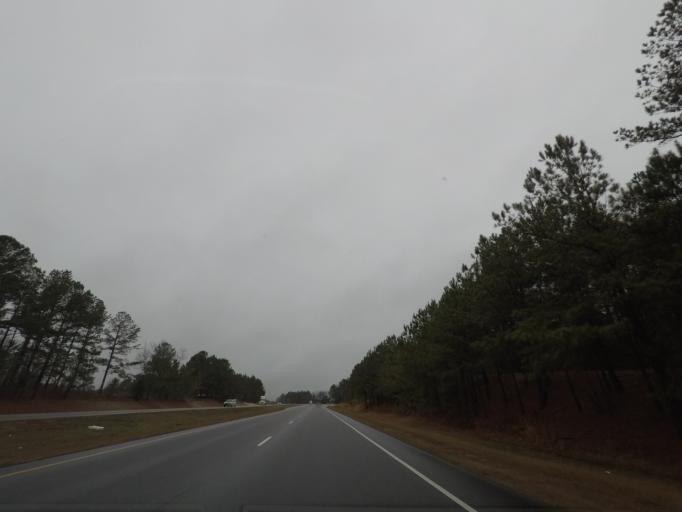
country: US
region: North Carolina
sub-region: Lee County
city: Broadway
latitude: 35.3301
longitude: -79.0940
